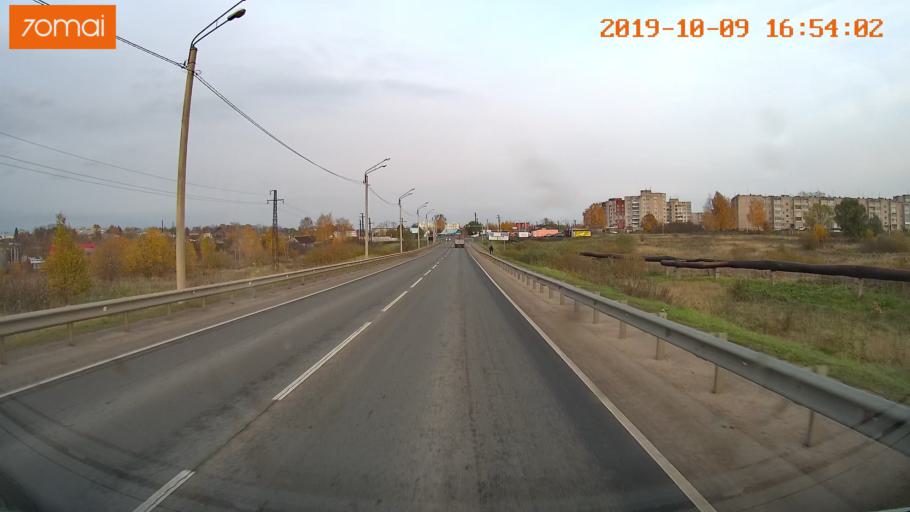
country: RU
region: Ivanovo
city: Privolzhsk
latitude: 57.3745
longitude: 41.2751
